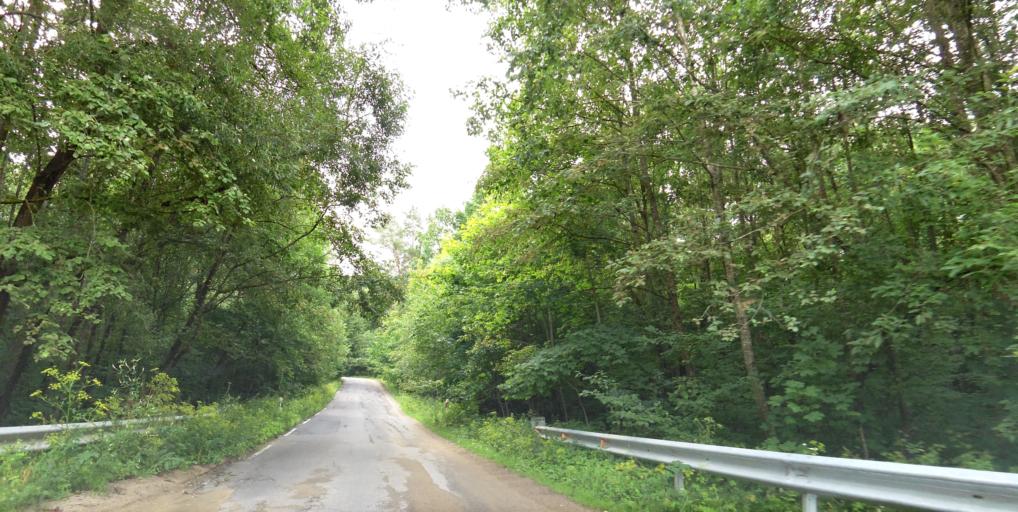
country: LT
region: Vilnius County
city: Pilaite
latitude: 54.6970
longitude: 25.1911
